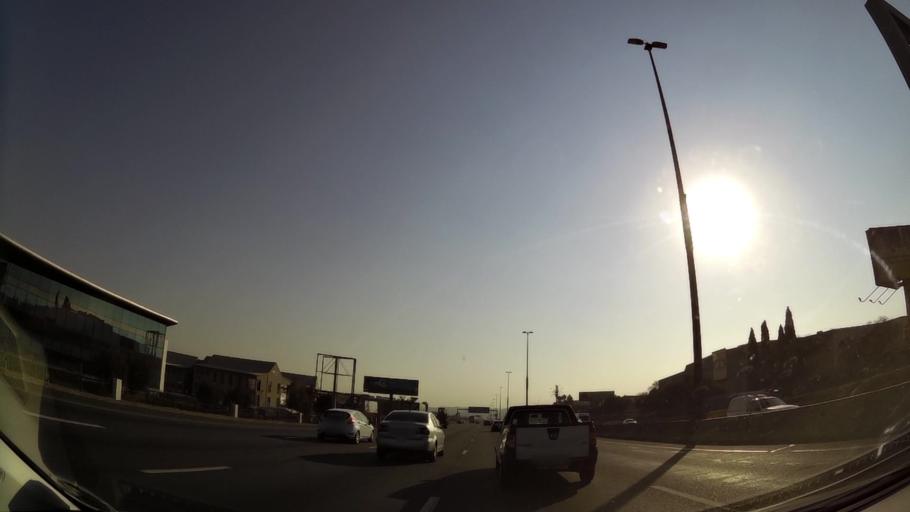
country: ZA
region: Gauteng
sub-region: City of Johannesburg Metropolitan Municipality
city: Midrand
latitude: -25.9650
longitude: 28.1307
